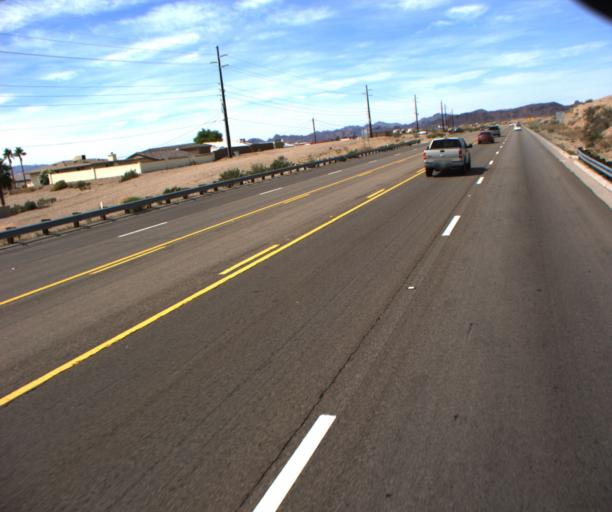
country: US
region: Arizona
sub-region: Mohave County
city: Desert Hills
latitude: 34.5227
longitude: -114.3495
